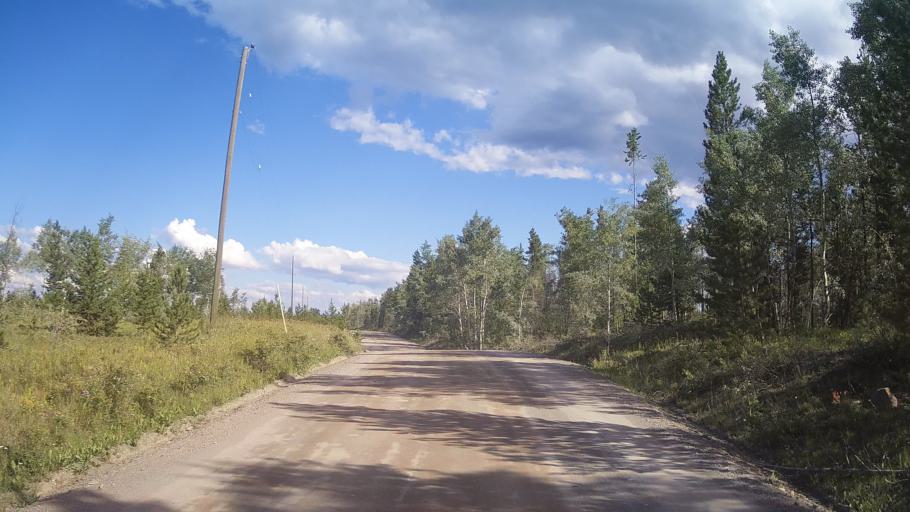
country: CA
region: British Columbia
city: Cache Creek
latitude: 51.2559
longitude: -121.6793
